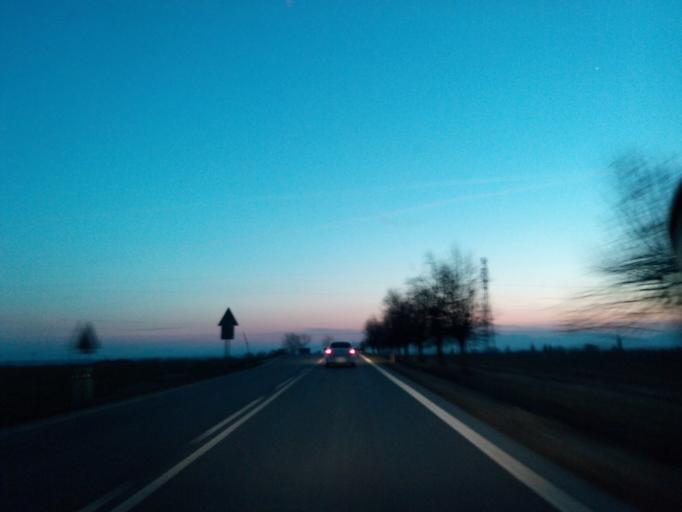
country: SK
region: Kosicky
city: Michalovce
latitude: 48.7007
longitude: 21.8141
